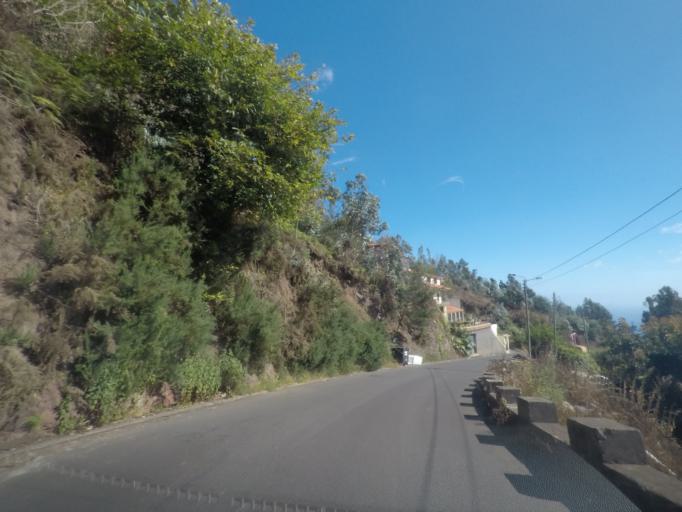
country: PT
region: Madeira
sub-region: Ribeira Brava
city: Campanario
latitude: 32.6863
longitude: -17.0216
